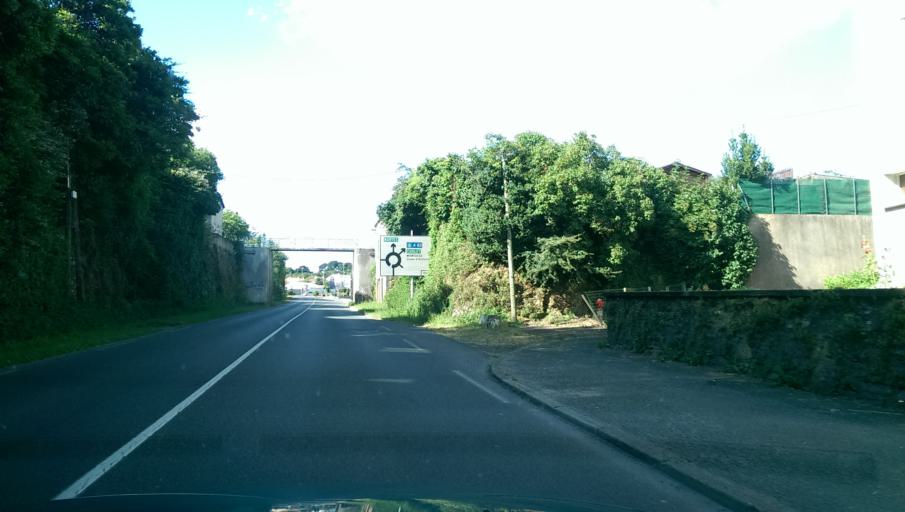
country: FR
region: Pays de la Loire
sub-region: Departement de la Vendee
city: Rocheserviere
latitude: 46.9367
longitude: -1.5143
